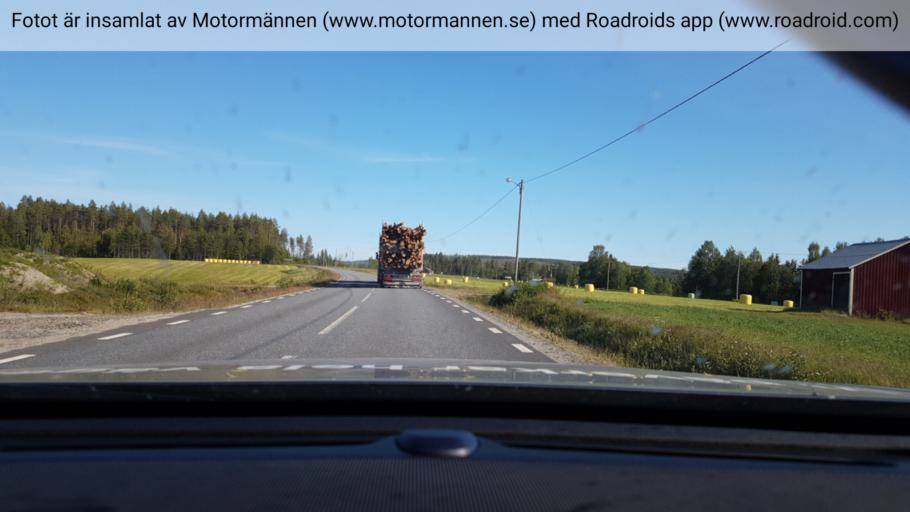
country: SE
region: Vaesterbotten
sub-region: Bjurholms Kommun
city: Bjurholm
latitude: 64.3038
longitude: 19.1668
